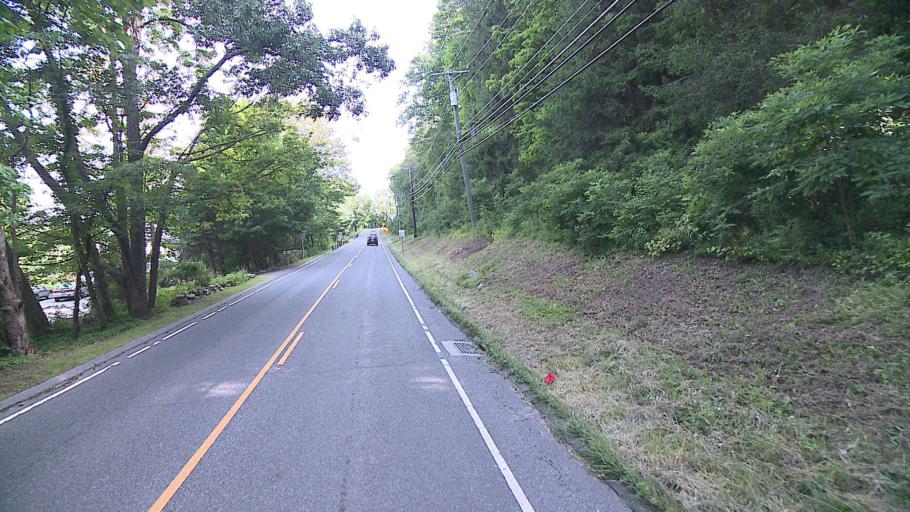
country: US
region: Connecticut
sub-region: Fairfield County
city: Sherman
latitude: 41.5866
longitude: -73.4795
